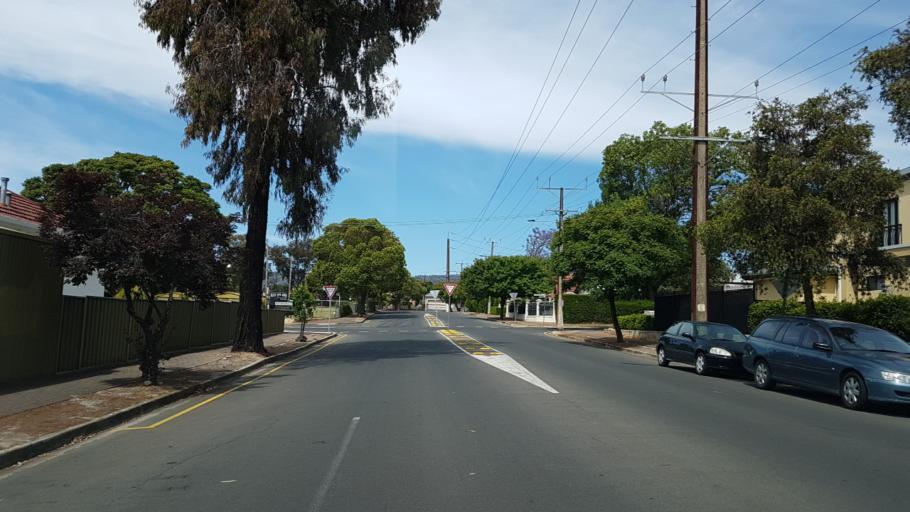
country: AU
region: South Australia
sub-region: Norwood Payneham St Peters
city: Trinity Gardens
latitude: -34.9119
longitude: 138.6467
